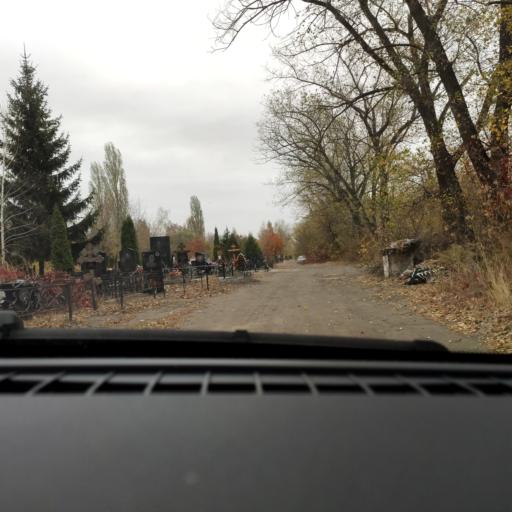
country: RU
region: Voronezj
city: Somovo
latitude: 51.6610
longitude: 39.2927
